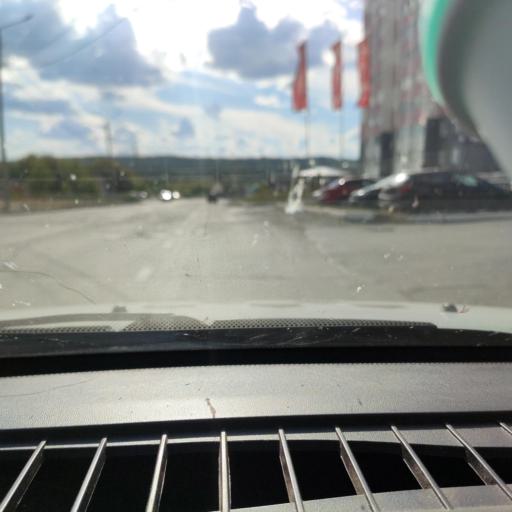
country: RU
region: Chelyabinsk
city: Miass
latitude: 55.0455
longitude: 60.0951
